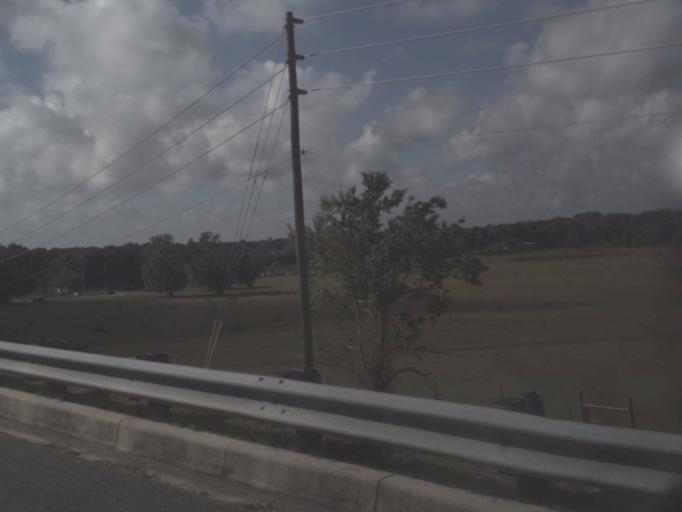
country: US
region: Florida
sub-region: Lake County
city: Lady Lake
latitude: 28.9297
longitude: -81.9280
